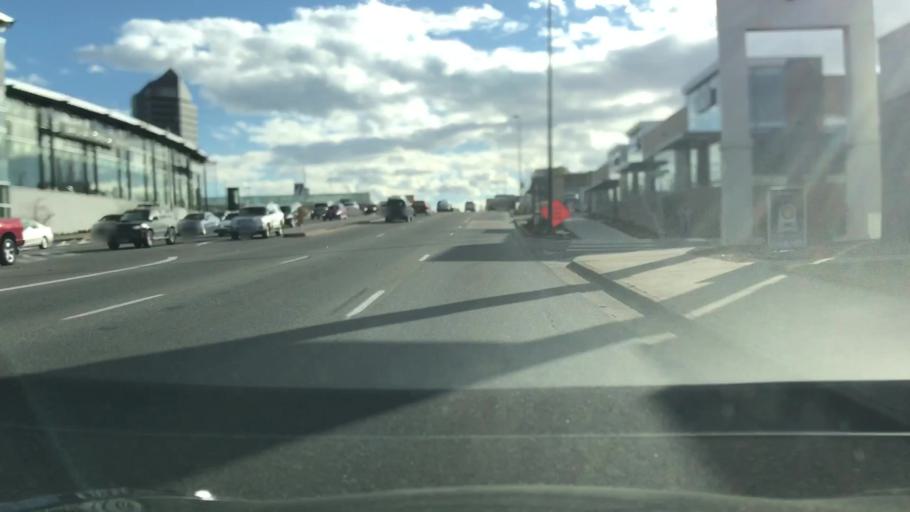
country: US
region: Colorado
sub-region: Arapahoe County
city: Glendale
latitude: 39.7004
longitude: -104.9408
